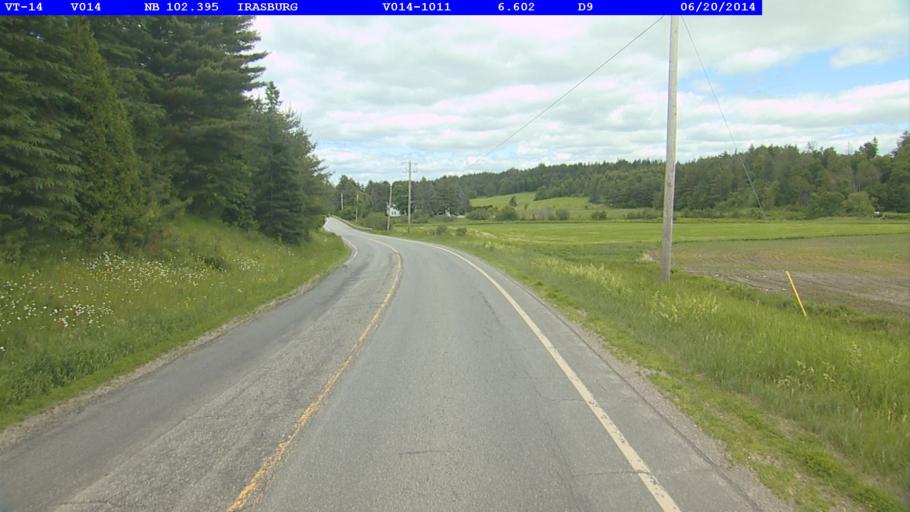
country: US
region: Vermont
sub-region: Orleans County
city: Newport
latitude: 44.8510
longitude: -72.2768
